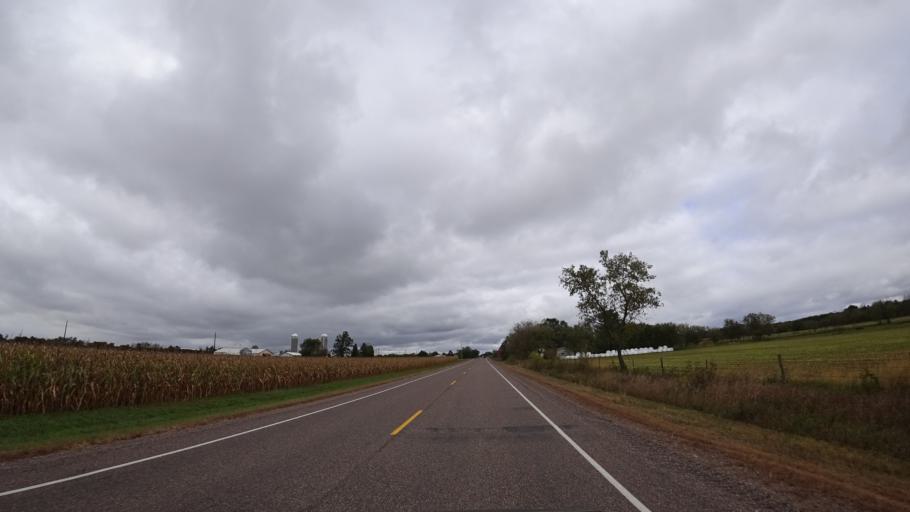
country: US
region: Wisconsin
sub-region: Chippewa County
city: Lake Wissota
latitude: 45.0059
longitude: -91.2867
